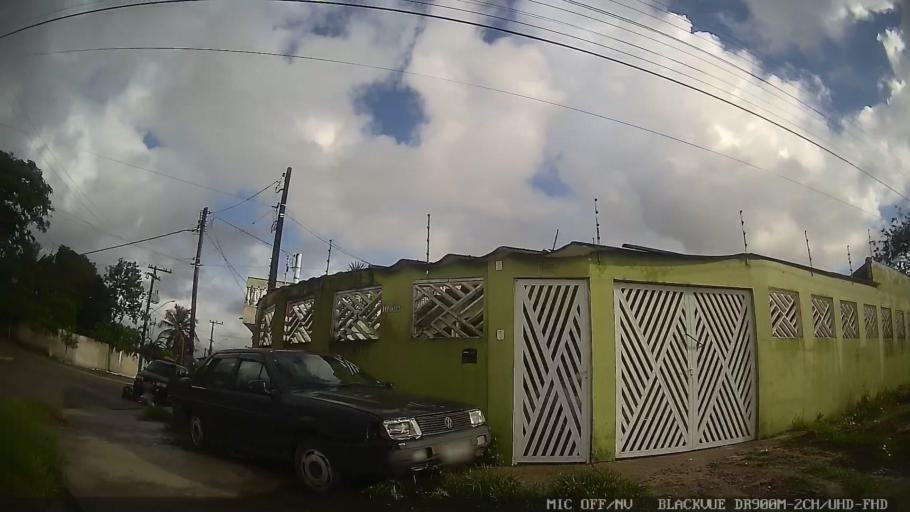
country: BR
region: Sao Paulo
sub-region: Itanhaem
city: Itanhaem
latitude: -24.1788
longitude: -46.8532
